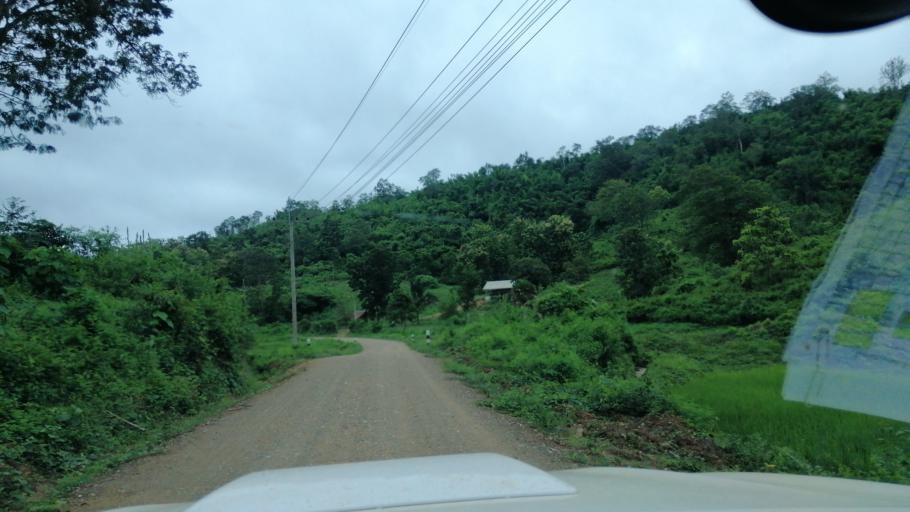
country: LA
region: Xiagnabouli
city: Muang Kenthao
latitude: 17.9417
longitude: 101.3927
